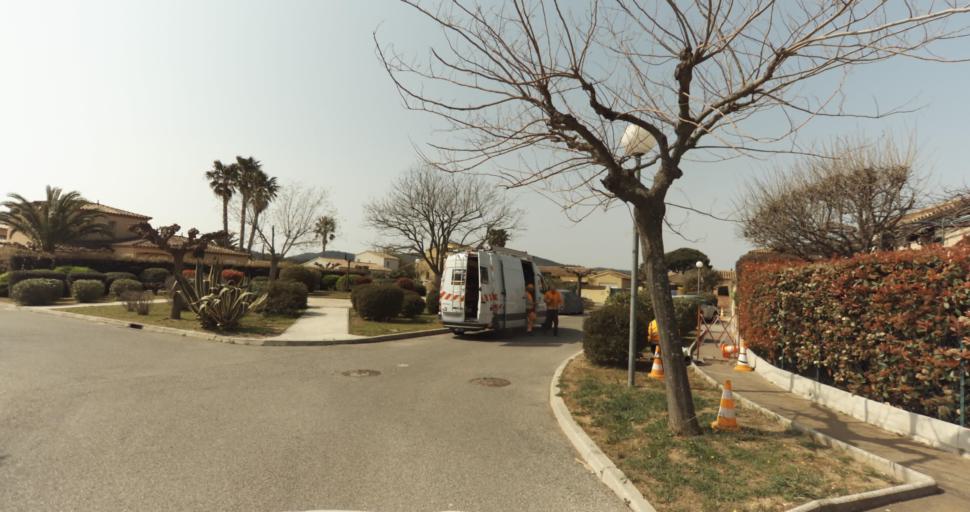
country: FR
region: Provence-Alpes-Cote d'Azur
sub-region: Departement du Var
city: Bormes-les-Mimosas
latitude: 43.1355
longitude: 6.3424
